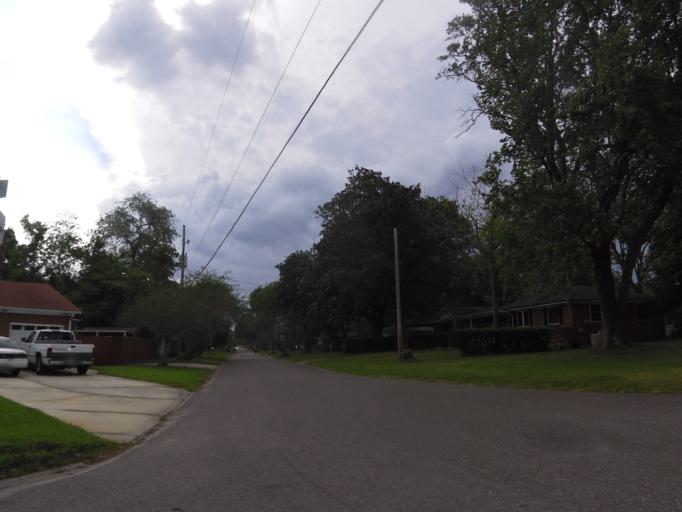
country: US
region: Florida
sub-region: Duval County
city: Jacksonville
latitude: 30.2981
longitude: -81.7323
